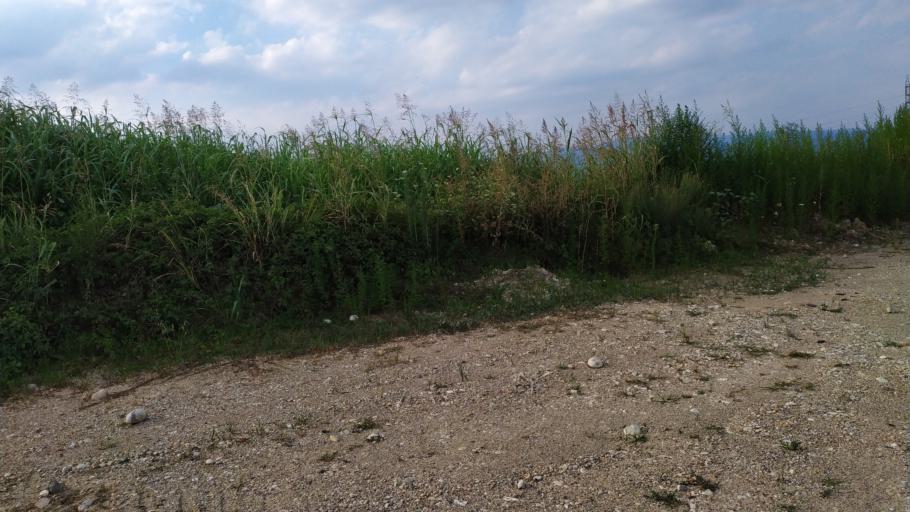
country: IT
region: Veneto
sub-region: Provincia di Vicenza
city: Isola Vicentina
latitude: 45.6511
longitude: 11.4380
